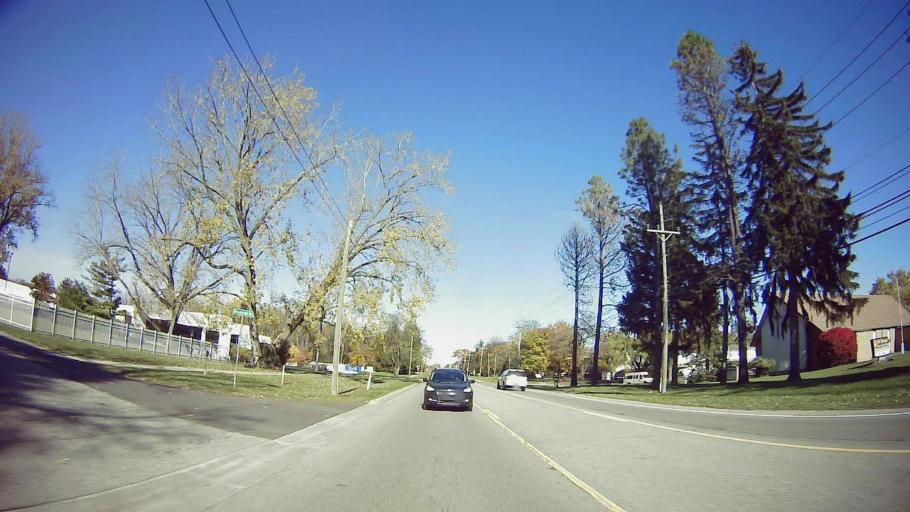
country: US
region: Michigan
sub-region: Oakland County
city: Southfield
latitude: 42.4638
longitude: -83.2604
